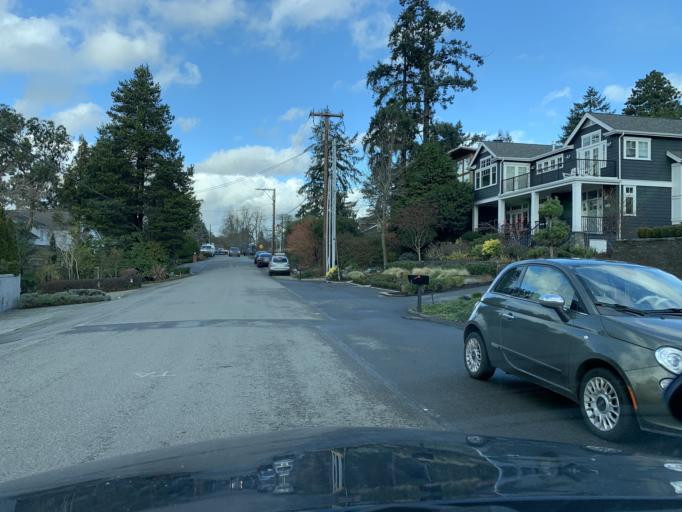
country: US
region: Washington
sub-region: King County
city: Mercer Island
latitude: 47.5864
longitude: -122.2527
